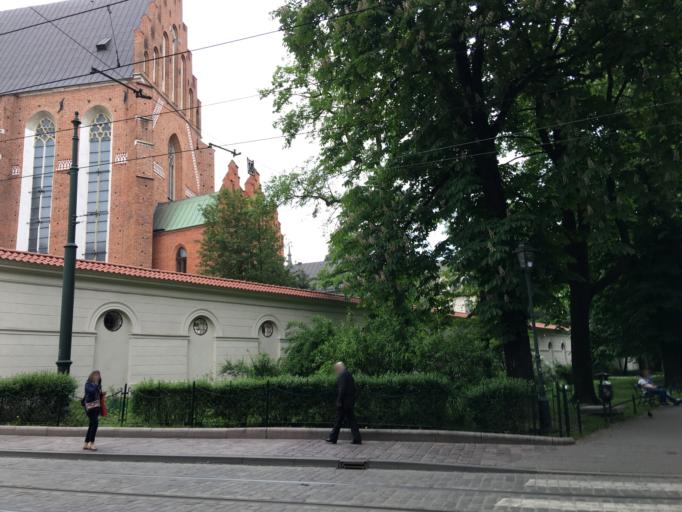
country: PL
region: Lesser Poland Voivodeship
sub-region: Krakow
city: Krakow
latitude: 50.0589
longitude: 19.9404
